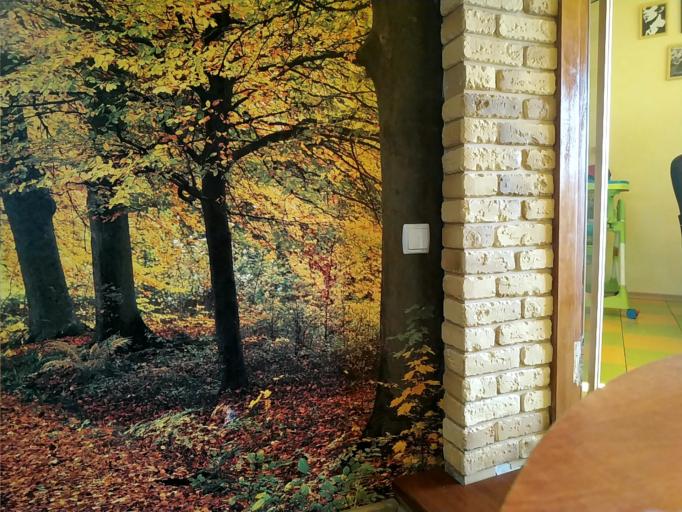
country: RU
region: Vologda
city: Nelazskoye
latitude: 59.4011
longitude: 37.6091
